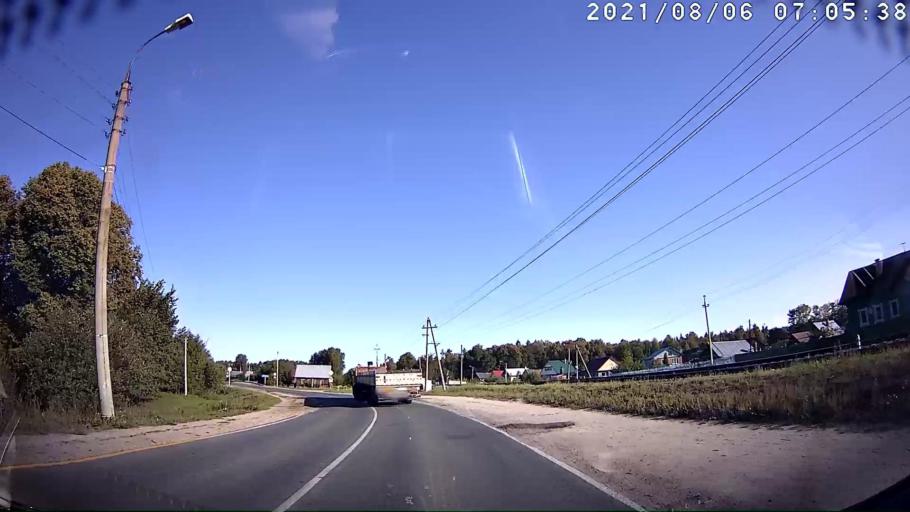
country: RU
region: Mariy-El
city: Yoshkar-Ola
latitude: 56.5547
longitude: 47.9862
